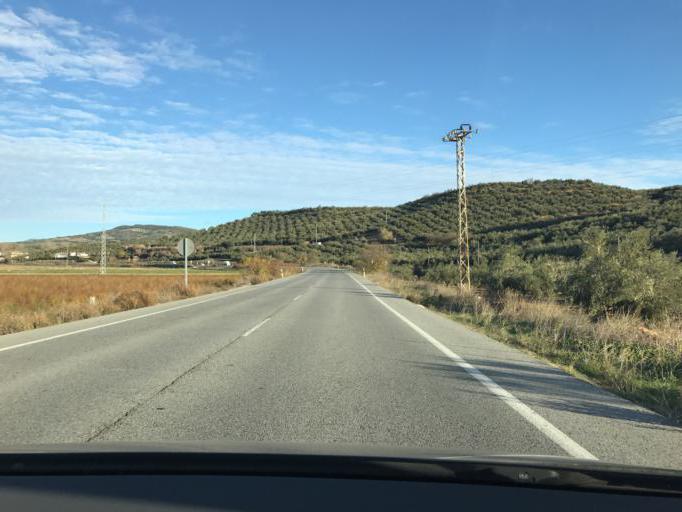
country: ES
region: Andalusia
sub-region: Provincia de Granada
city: Iznalloz
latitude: 37.4059
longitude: -3.5068
